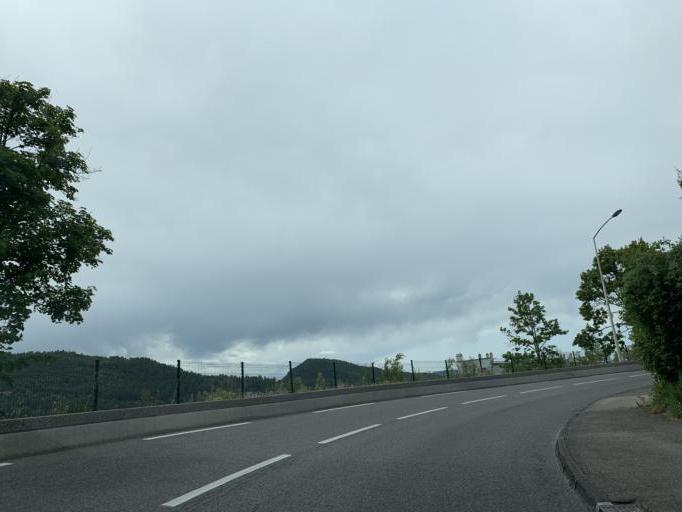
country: FR
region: Provence-Alpes-Cote d'Azur
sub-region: Departement des Hautes-Alpes
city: Gap
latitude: 44.5577
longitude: 6.0716
